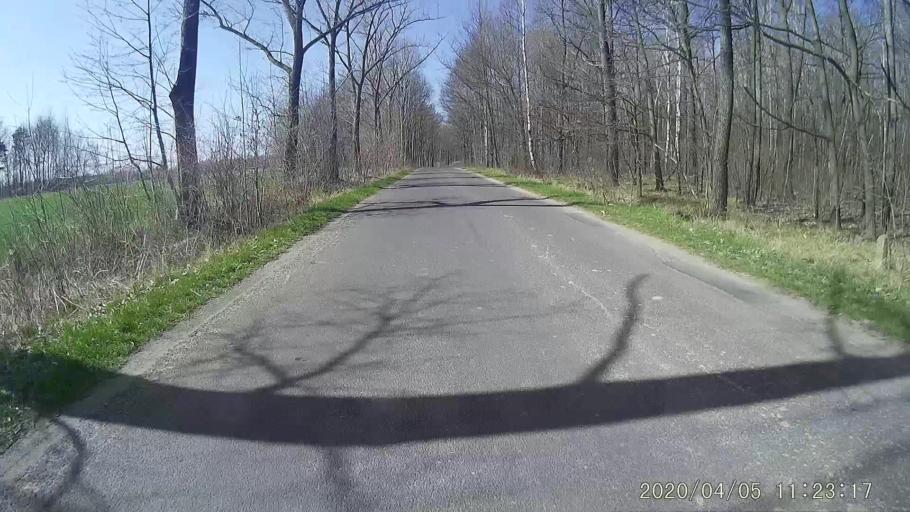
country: PL
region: Lower Silesian Voivodeship
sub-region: Powiat zgorzelecki
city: Sulikow
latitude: 51.0538
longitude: 15.1435
